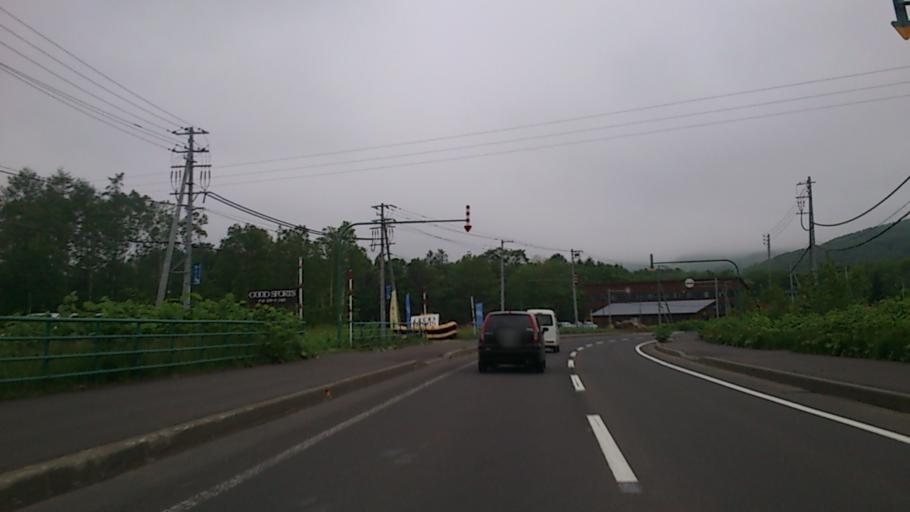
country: JP
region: Hokkaido
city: Niseko Town
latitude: 42.8635
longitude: 140.7228
